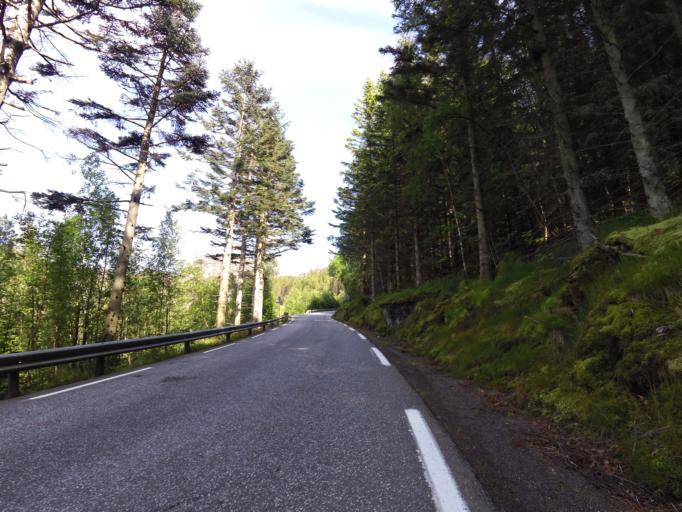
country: NO
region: Rogaland
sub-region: Sokndal
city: Hauge i Dalane
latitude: 58.3143
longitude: 6.3439
